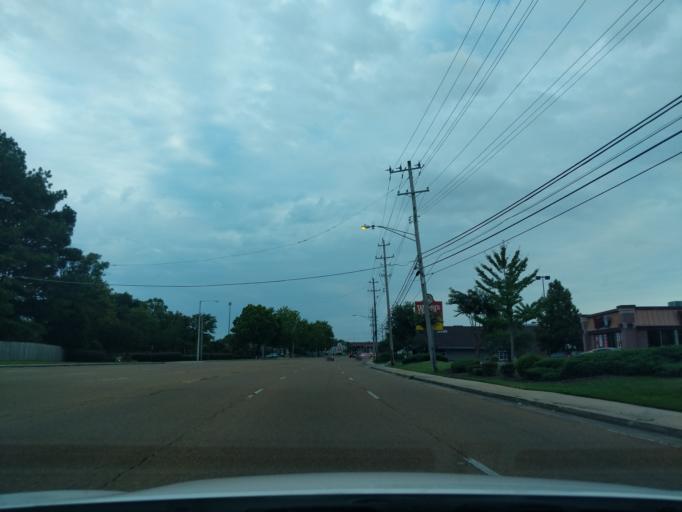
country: US
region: Tennessee
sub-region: Shelby County
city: Germantown
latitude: 35.0717
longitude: -89.8426
